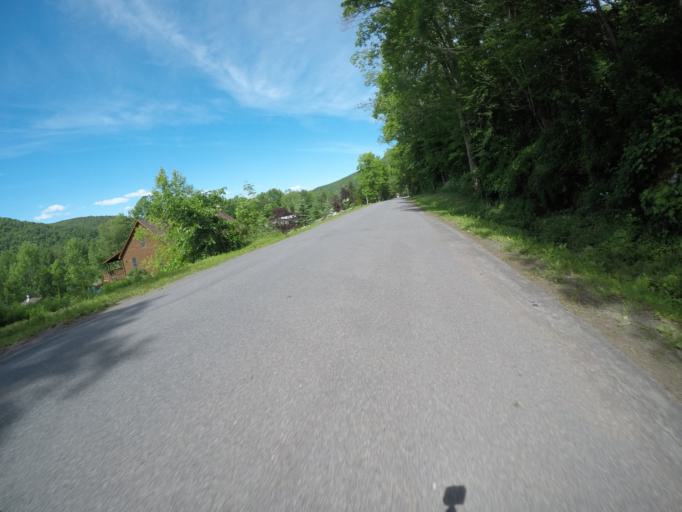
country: US
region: New York
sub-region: Delaware County
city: Stamford
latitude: 42.1314
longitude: -74.6624
